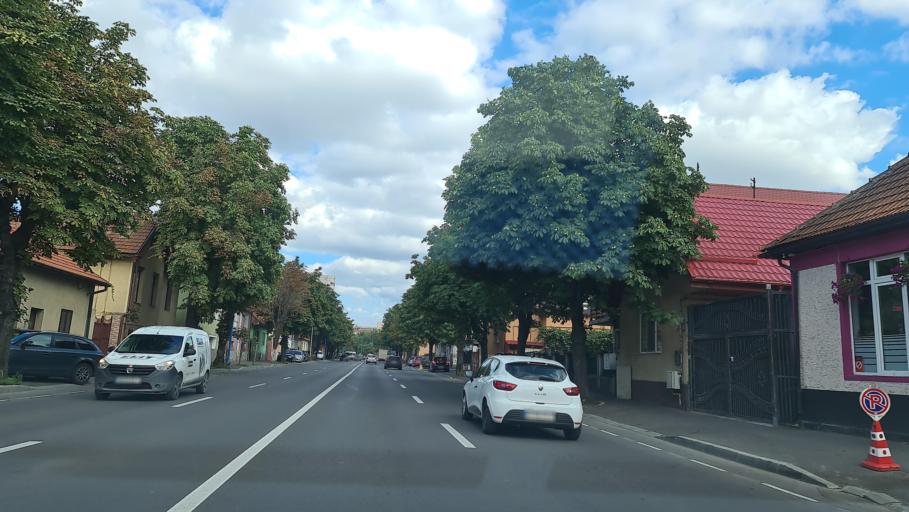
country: RO
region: Brasov
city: Brasov
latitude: 45.6602
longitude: 25.6029
